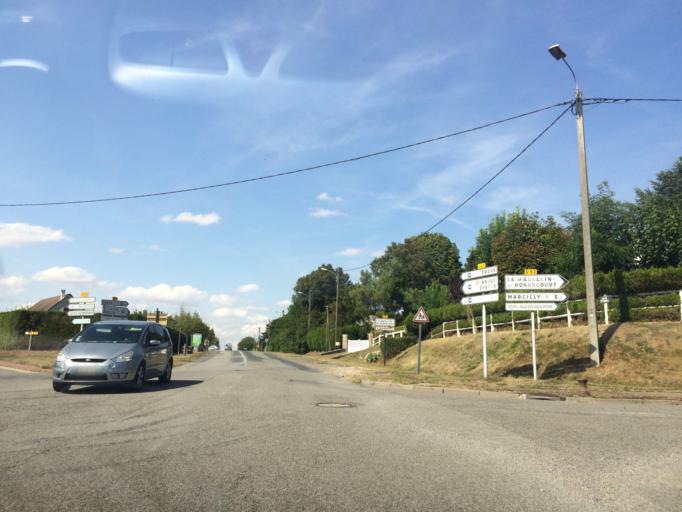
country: FR
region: Haute-Normandie
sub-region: Departement de l'Eure
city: Nonancourt
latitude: 48.7751
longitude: 1.1948
